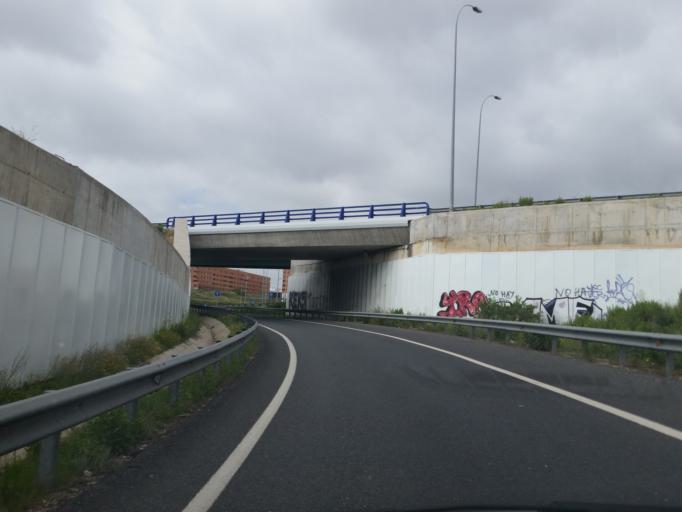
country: ES
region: Andalusia
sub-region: Provincia de Malaga
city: Malaga
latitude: 36.7140
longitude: -4.4565
